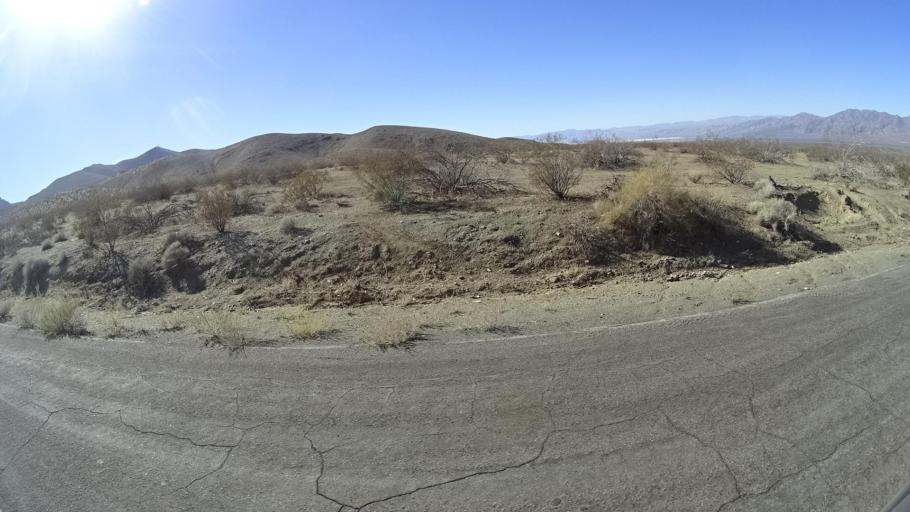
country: US
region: California
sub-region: Kern County
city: Ridgecrest
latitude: 35.3823
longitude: -117.6611
